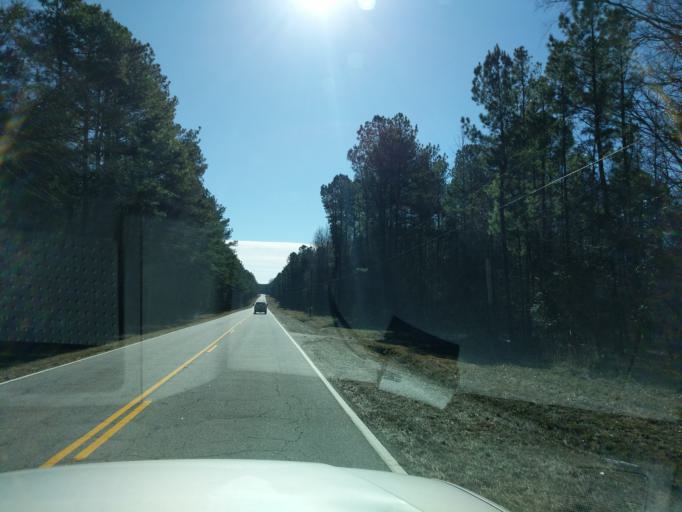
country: US
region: South Carolina
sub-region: Saluda County
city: Saluda
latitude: 34.1342
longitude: -81.8425
